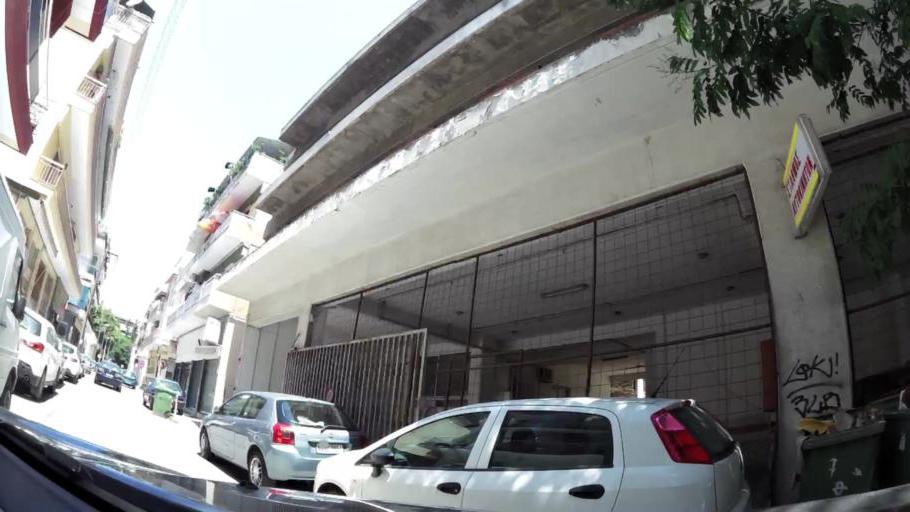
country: GR
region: Central Macedonia
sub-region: Nomos Thessalonikis
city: Triandria
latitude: 40.6063
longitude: 22.9551
